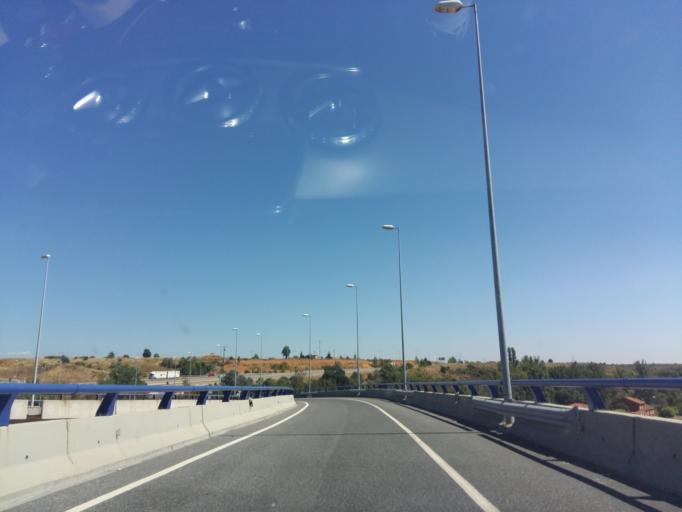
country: ES
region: Castille and Leon
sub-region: Provincia de Leon
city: Valverde de la Virgen
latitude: 42.5672
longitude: -5.6549
